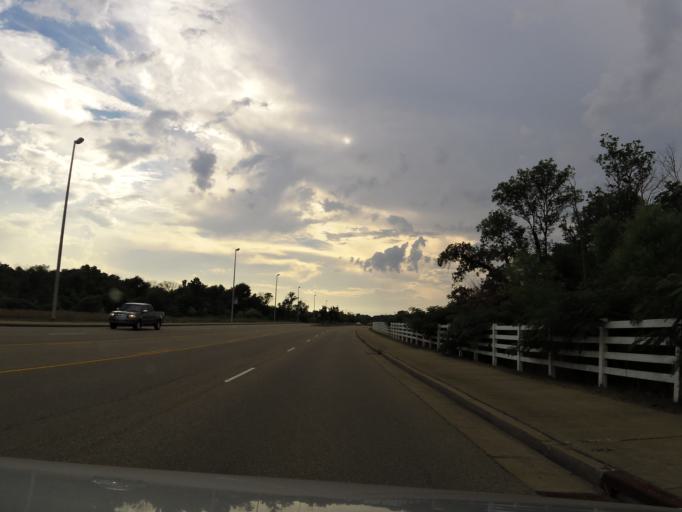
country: US
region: Tennessee
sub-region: Knox County
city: Farragut
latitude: 35.8769
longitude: -84.1509
